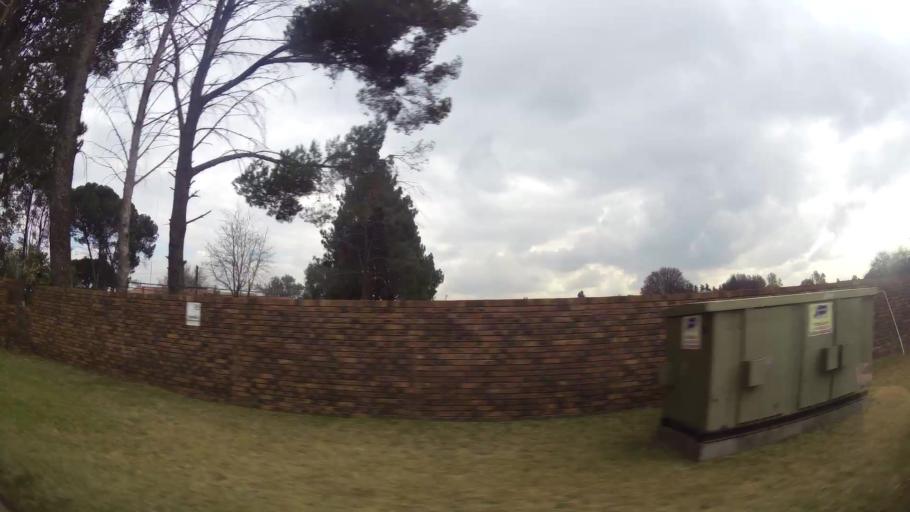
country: ZA
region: Gauteng
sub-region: Sedibeng District Municipality
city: Meyerton
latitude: -26.5879
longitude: 27.9982
